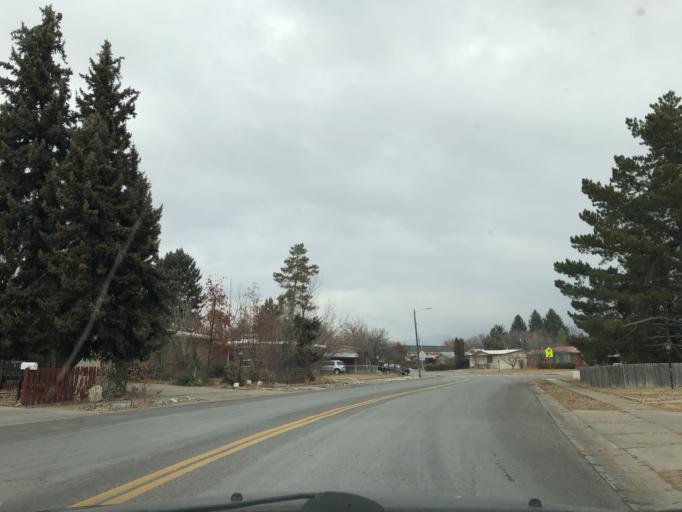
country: US
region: Utah
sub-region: Cache County
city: Logan
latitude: 41.7440
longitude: -111.8372
